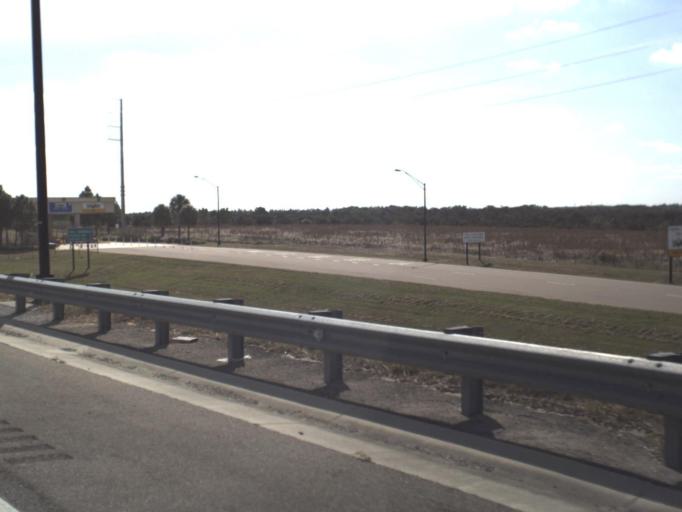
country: US
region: Florida
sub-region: Polk County
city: Citrus Ridge
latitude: 28.4189
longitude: -81.6321
